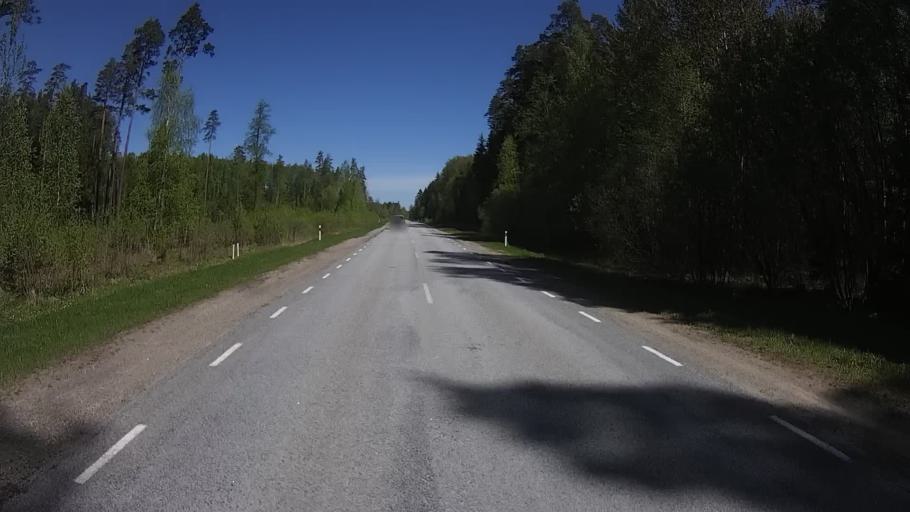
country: EE
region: Polvamaa
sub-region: Raepina vald
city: Rapina
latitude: 58.0616
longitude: 27.3938
